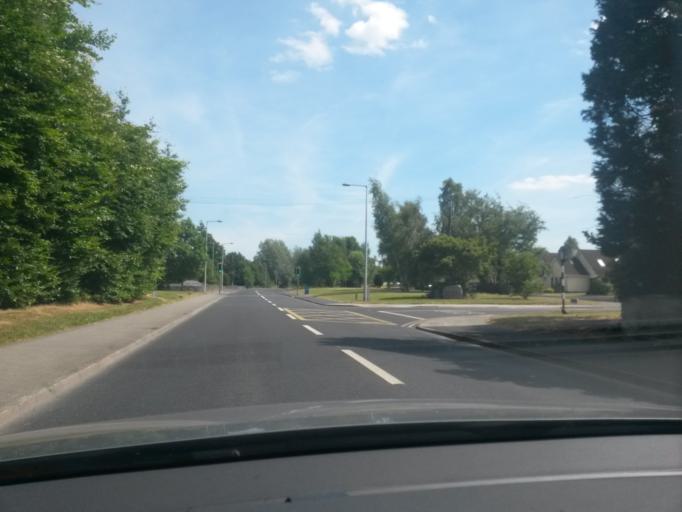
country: IE
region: Leinster
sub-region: Kildare
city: Naas
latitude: 53.2166
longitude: -6.6539
